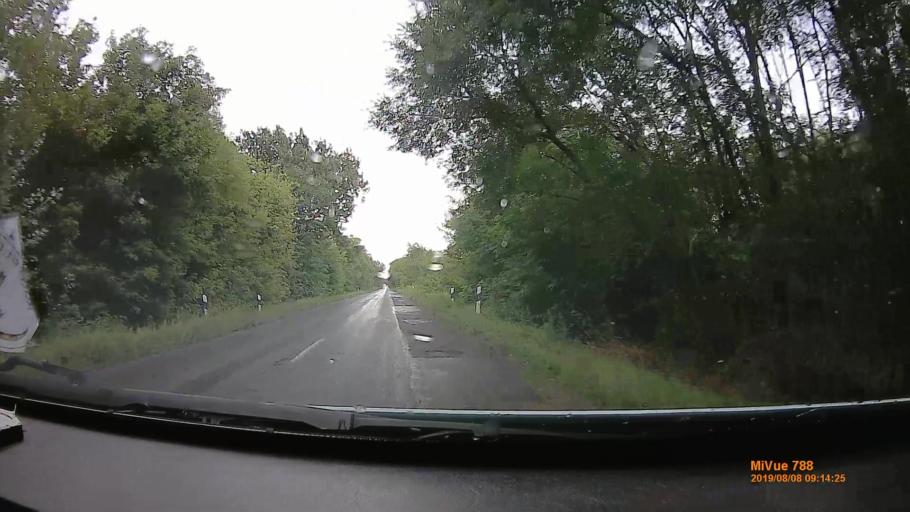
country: HU
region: Hajdu-Bihar
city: Hajdusamson
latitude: 47.5259
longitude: 21.7491
